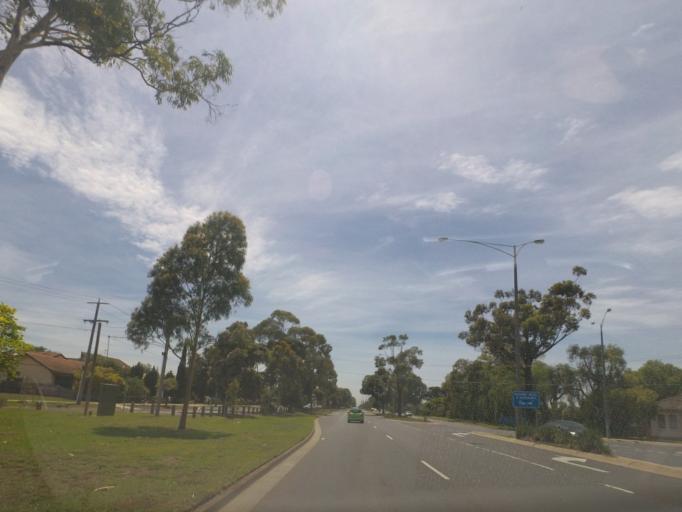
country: AU
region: Victoria
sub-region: Wyndham
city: Werribee
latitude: -37.9002
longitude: 144.6667
